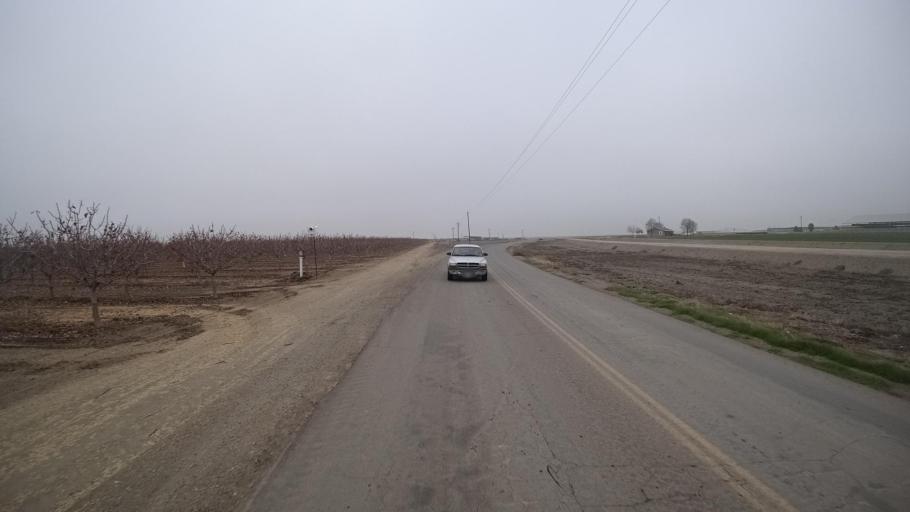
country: US
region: California
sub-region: Kern County
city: Rosedale
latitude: 35.2092
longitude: -119.2112
